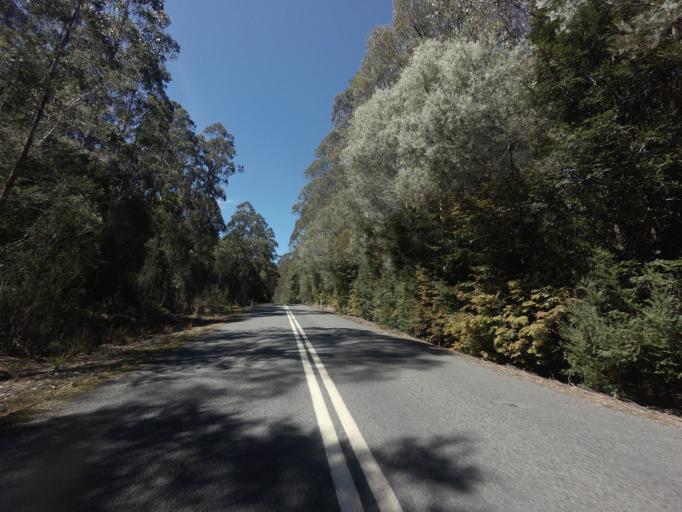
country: AU
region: Tasmania
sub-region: Huon Valley
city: Geeveston
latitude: -42.8224
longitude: 146.2784
